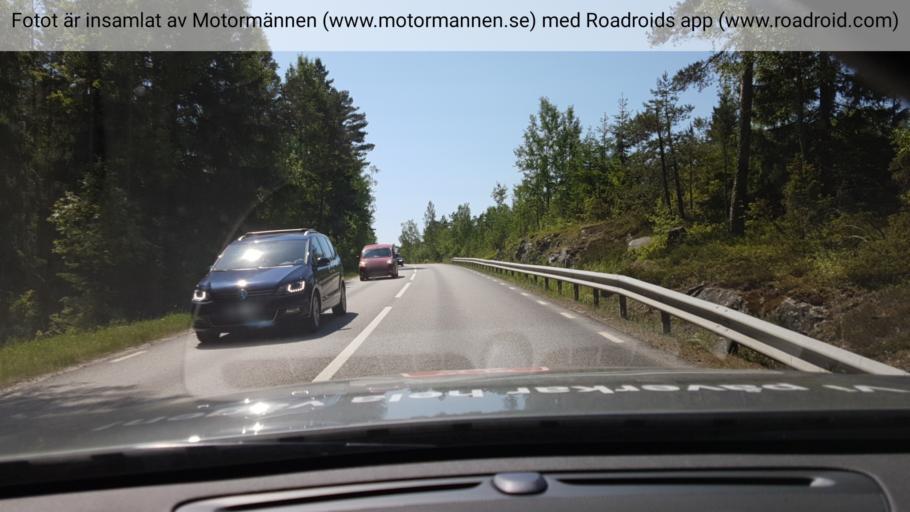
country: SE
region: Stockholm
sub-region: Norrtalje Kommun
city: Rimbo
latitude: 59.6696
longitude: 18.3516
